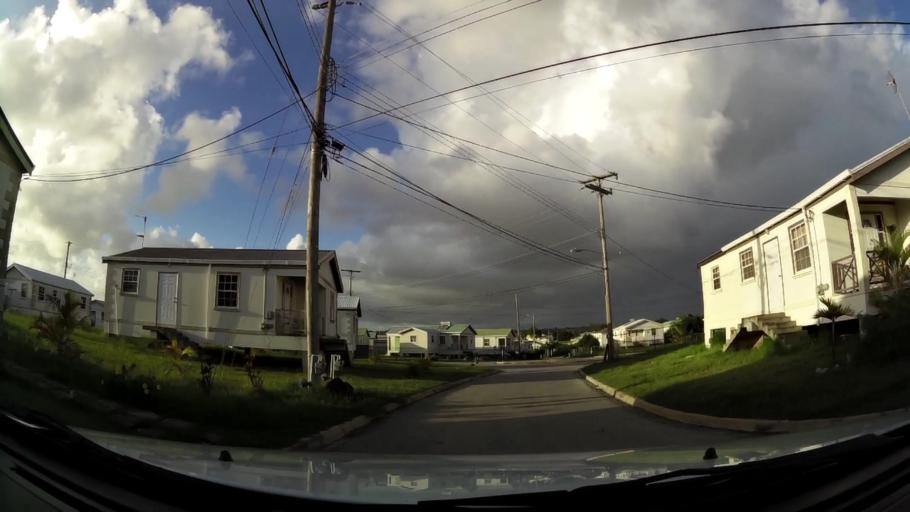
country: BB
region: Saint Philip
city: Crane
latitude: 13.1136
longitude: -59.4770
